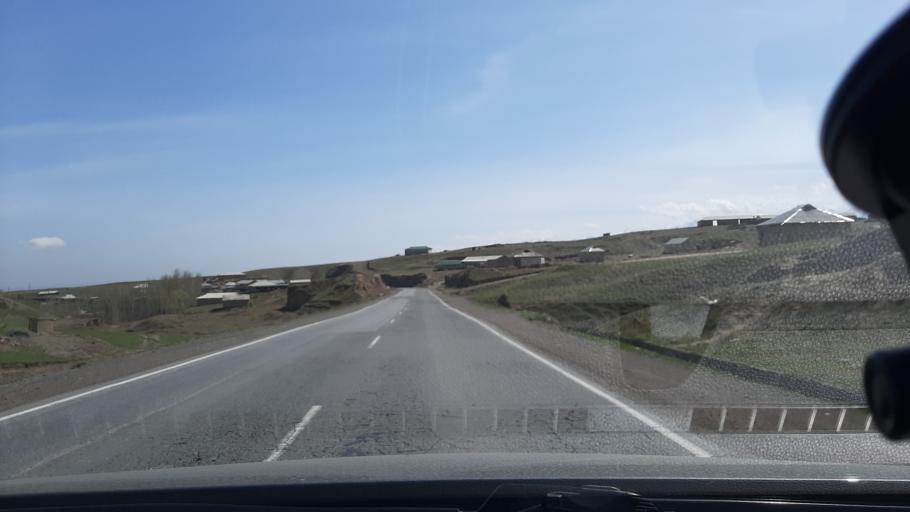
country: TJ
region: Viloyati Sughd
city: Shahriston
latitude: 39.7625
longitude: 68.8095
